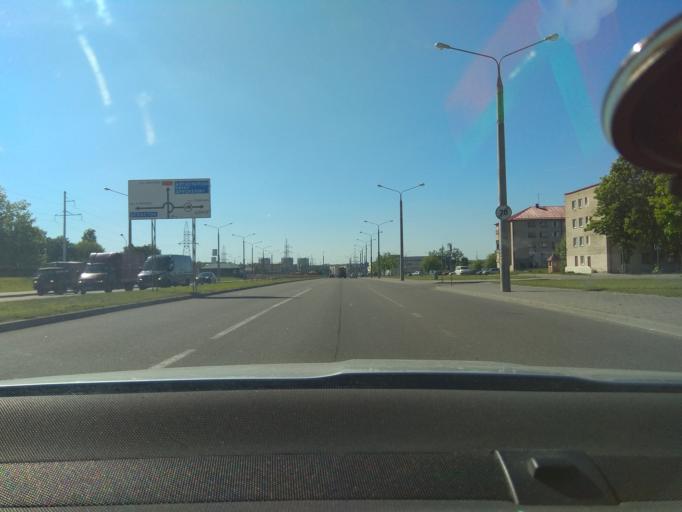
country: BY
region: Grodnenskaya
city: Hrodna
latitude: 53.6518
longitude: 23.7969
